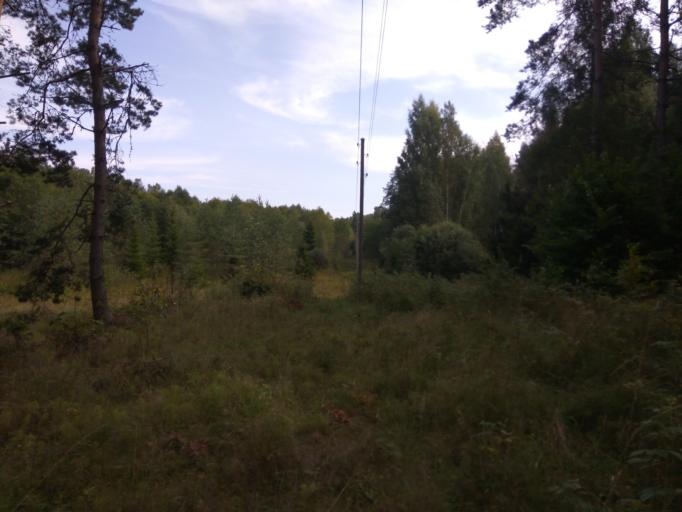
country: LV
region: Alsunga
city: Alsunga
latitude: 56.9840
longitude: 21.6818
